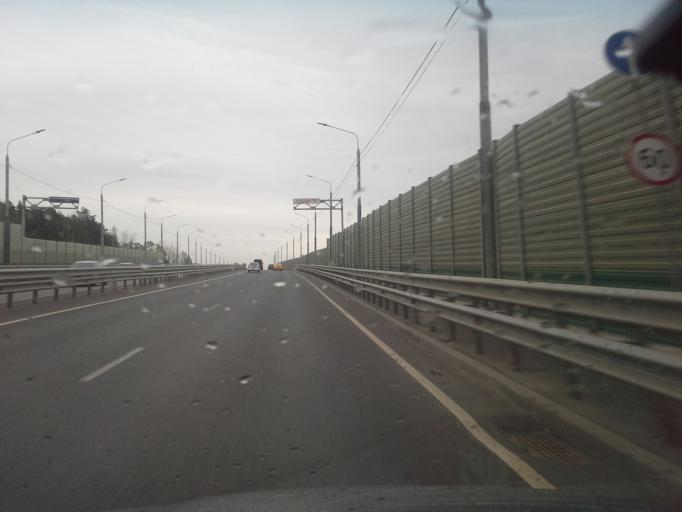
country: RU
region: Moskovskaya
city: Lesnoy Gorodok
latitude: 55.6541
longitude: 37.1596
